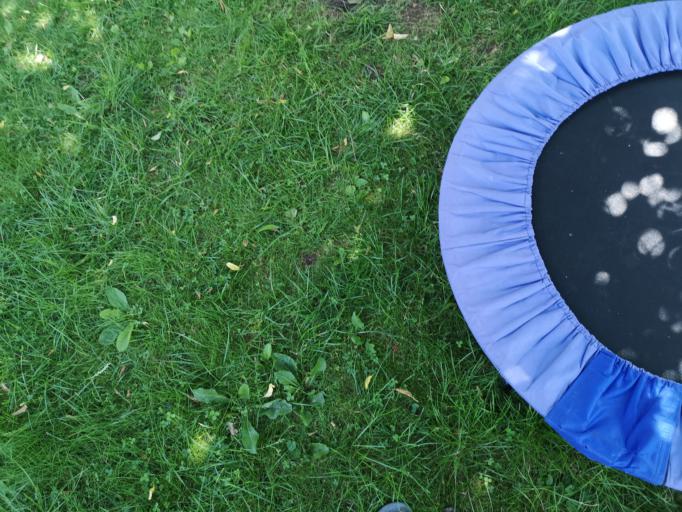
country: PL
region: Kujawsko-Pomorskie
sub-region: Powiat bydgoski
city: Biale Blota
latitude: 53.0242
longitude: 17.8646
